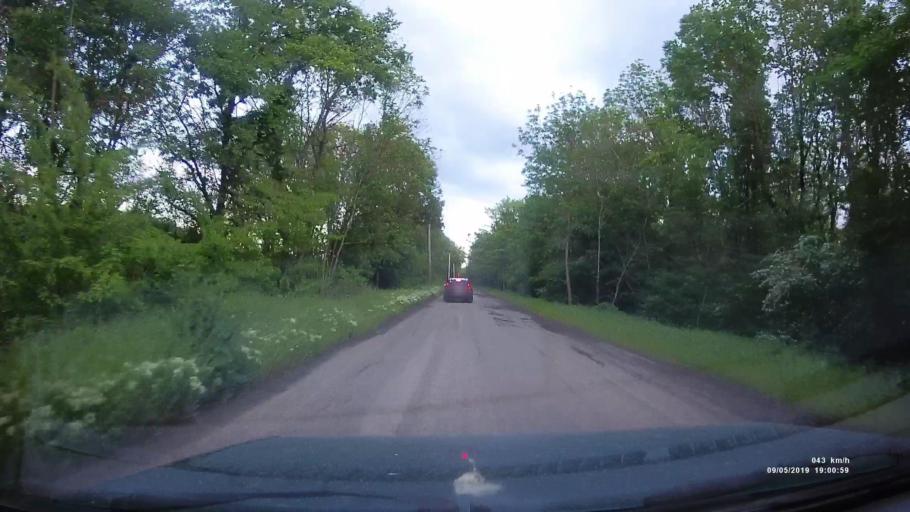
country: RU
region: Krasnodarskiy
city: Kanelovskaya
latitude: 46.7498
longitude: 39.1405
